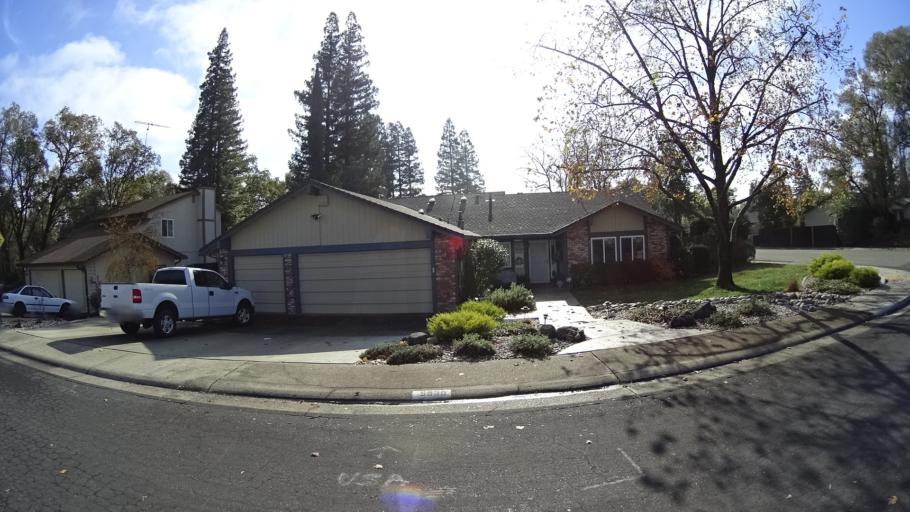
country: US
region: California
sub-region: Sacramento County
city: Antelope
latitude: 38.6843
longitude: -121.3252
